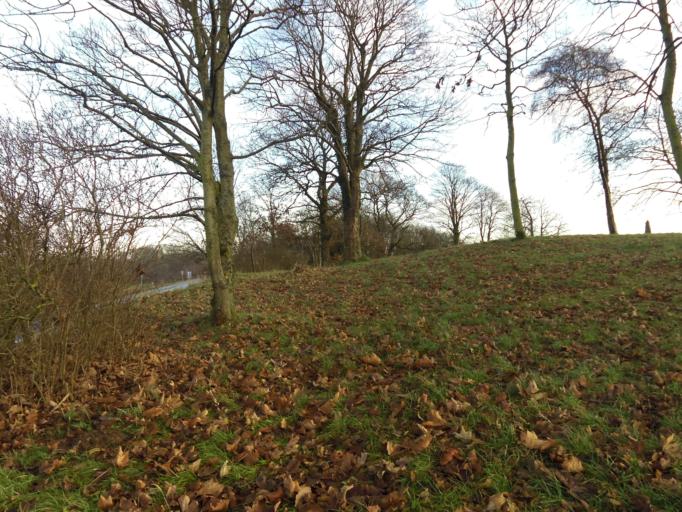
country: DK
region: South Denmark
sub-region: Haderslev Kommune
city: Gram
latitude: 55.2842
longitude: 8.9684
